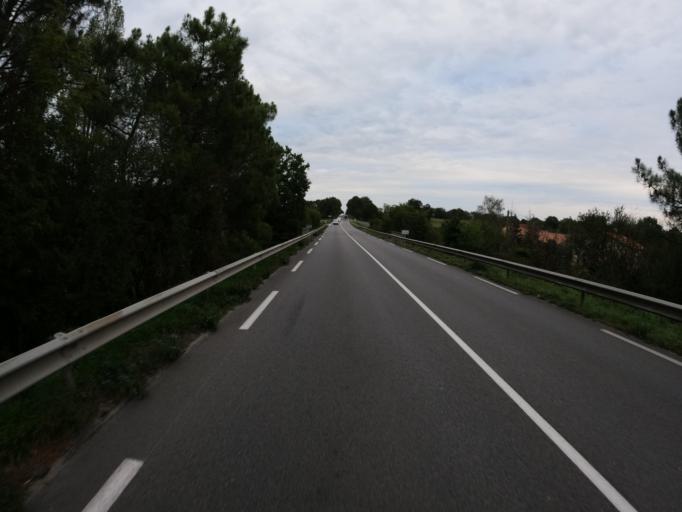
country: FR
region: Poitou-Charentes
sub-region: Departement des Deux-Sevres
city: La Peyratte
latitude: 46.6489
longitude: -0.1871
